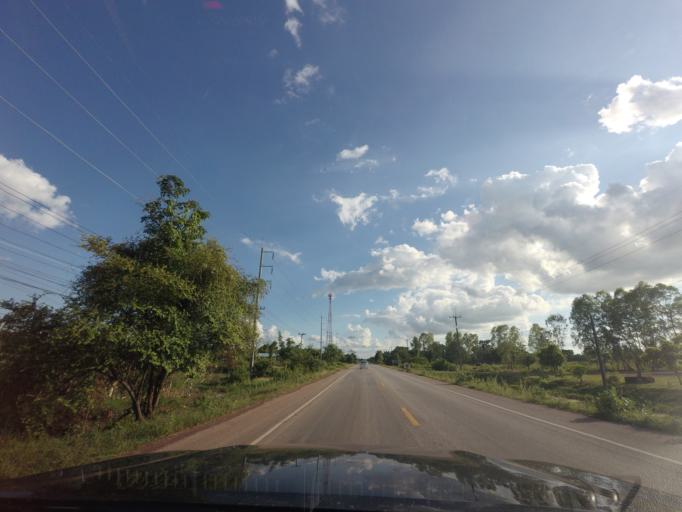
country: TH
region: Changwat Udon Thani
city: Thung Fon
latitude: 17.4836
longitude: 103.1961
